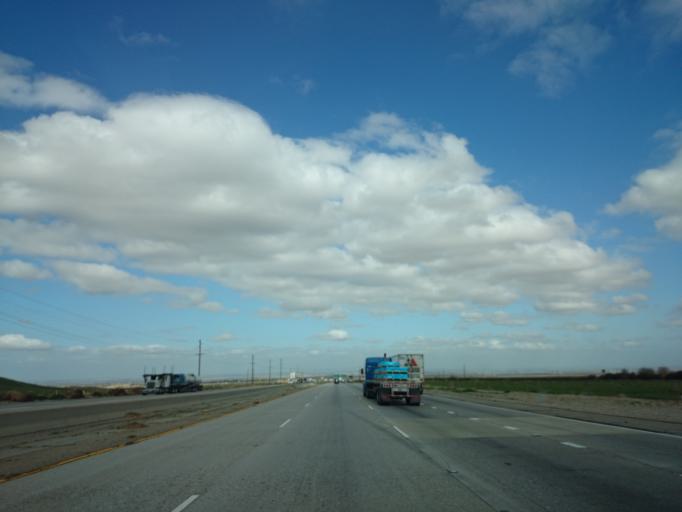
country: US
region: California
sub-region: Kern County
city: Frazier Park
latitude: 35.0003
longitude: -118.9496
